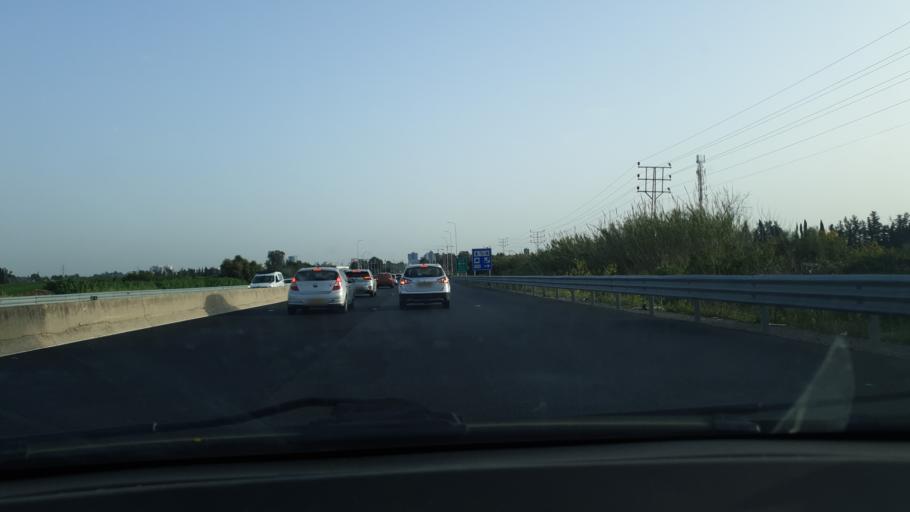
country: IL
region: Central District
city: Ra'anana
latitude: 32.2225
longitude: 34.8829
